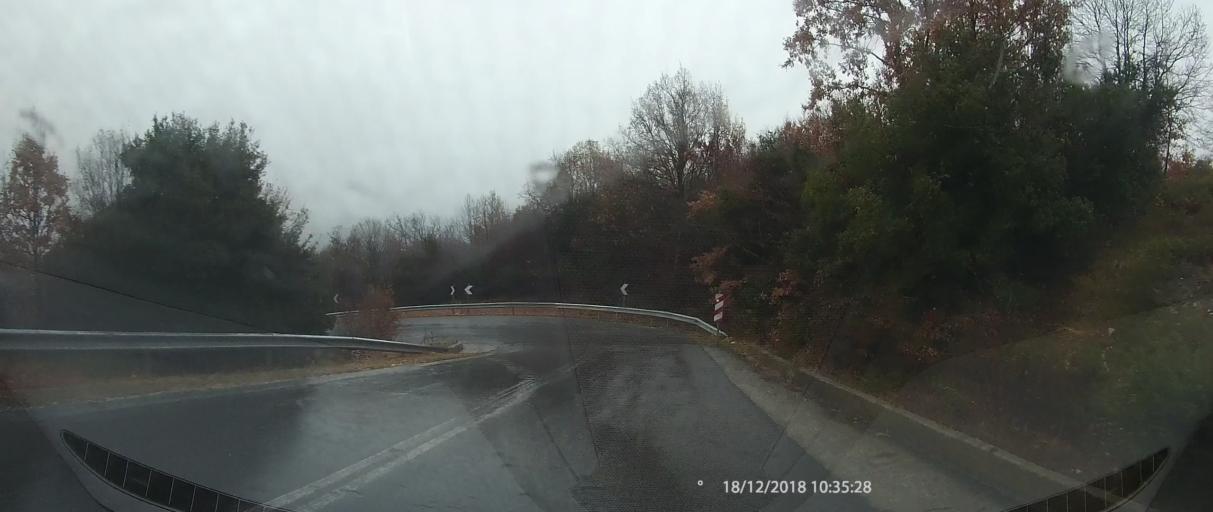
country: GR
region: Central Macedonia
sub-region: Nomos Pierias
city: Kato Milia
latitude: 40.2145
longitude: 22.3075
